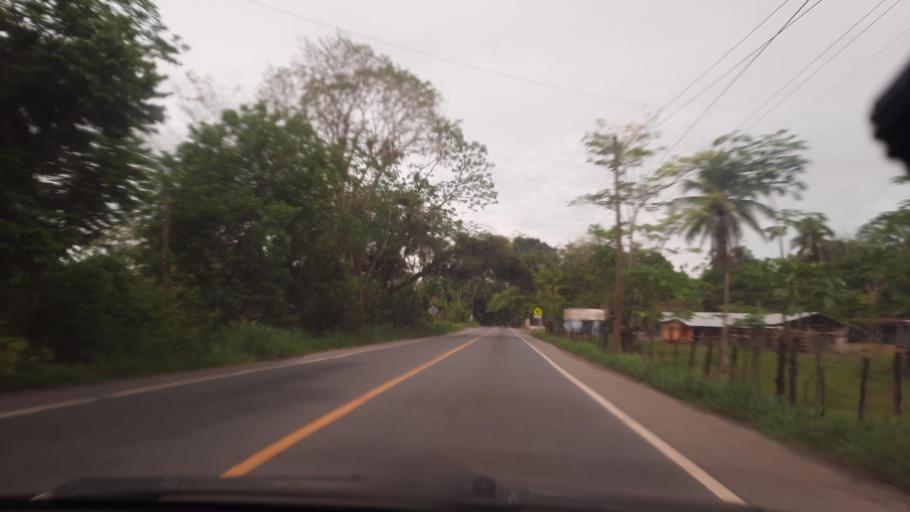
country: GT
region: Izabal
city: Morales
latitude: 15.5145
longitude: -88.7999
